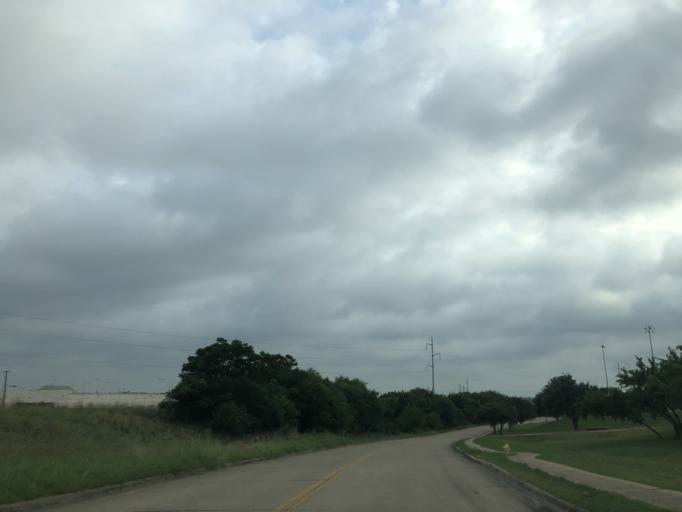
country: US
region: Texas
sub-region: Dallas County
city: Mesquite
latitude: 32.8329
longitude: -96.6287
